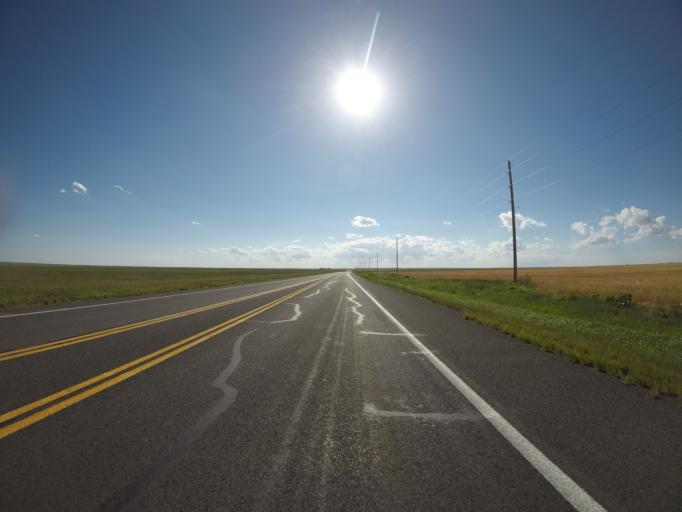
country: US
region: Colorado
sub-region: Morgan County
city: Brush
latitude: 40.6099
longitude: -103.6832
